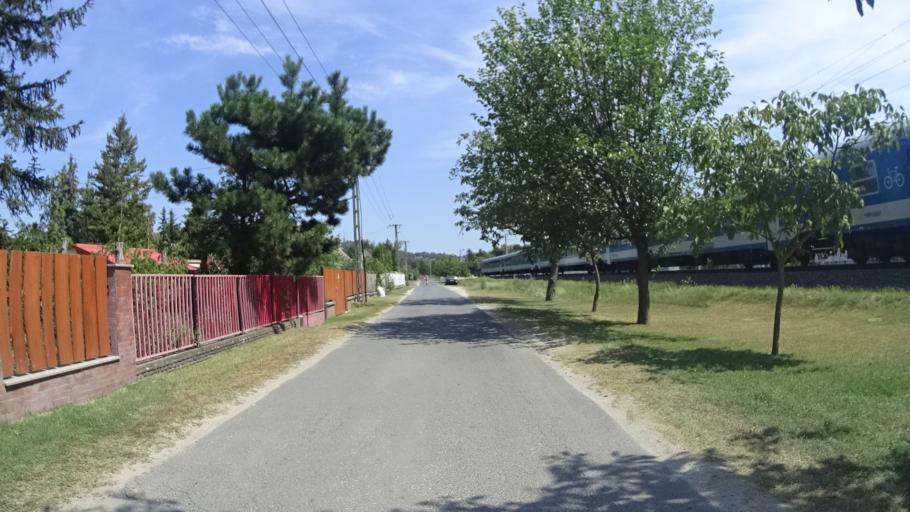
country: HU
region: Somogy
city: Balatonfenyves
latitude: 46.7274
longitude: 17.5241
